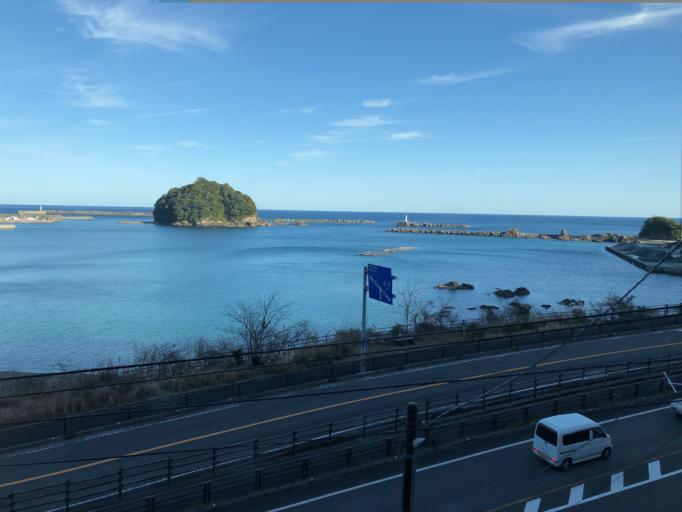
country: JP
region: Kochi
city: Nakamura
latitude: 33.0725
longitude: 133.1039
